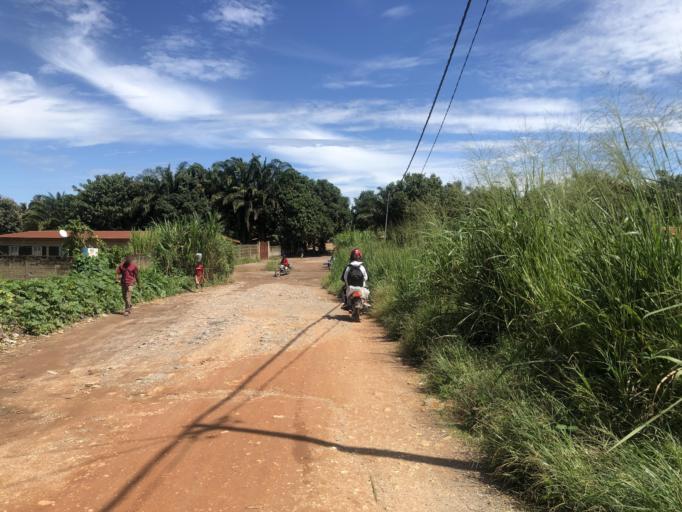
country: SL
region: Eastern Province
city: Koidu
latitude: 8.6437
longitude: -10.9546
